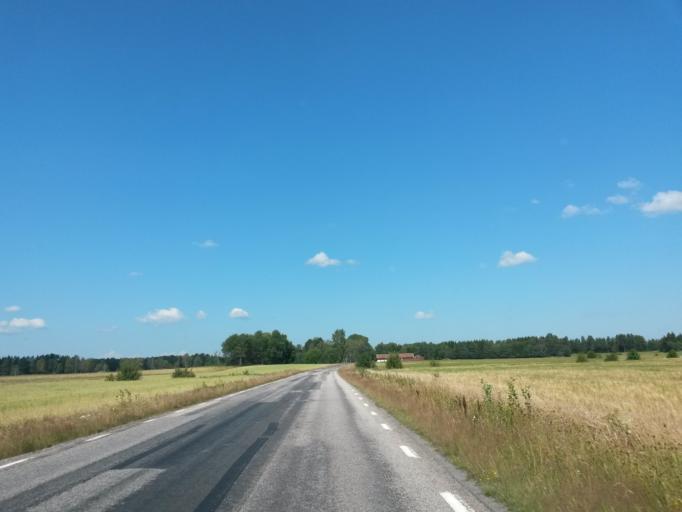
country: SE
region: Vaestra Goetaland
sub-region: Essunga Kommun
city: Nossebro
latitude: 58.1479
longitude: 12.7583
